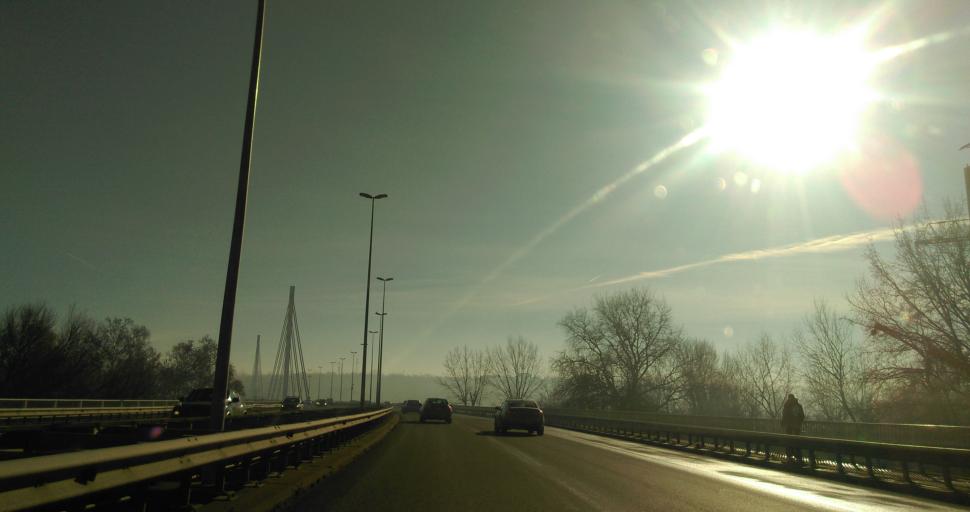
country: RS
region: Autonomna Pokrajina Vojvodina
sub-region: Juznobacki Okrug
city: Novi Sad
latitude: 45.2376
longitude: 19.8451
